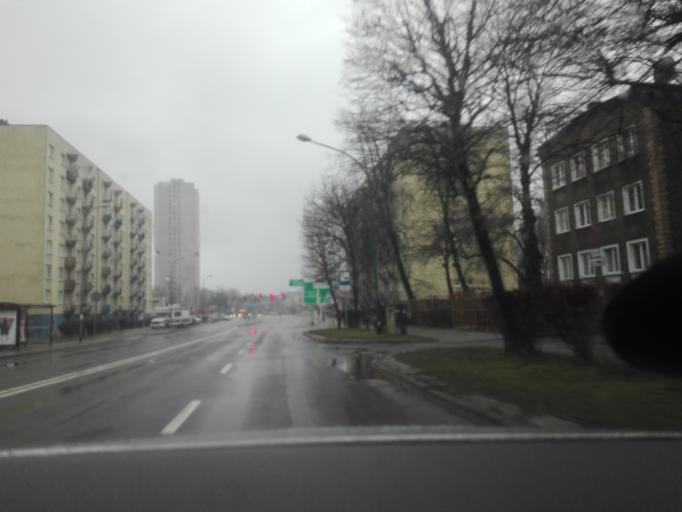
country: PL
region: Silesian Voivodeship
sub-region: Katowice
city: Katowice
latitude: 50.2671
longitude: 19.0198
